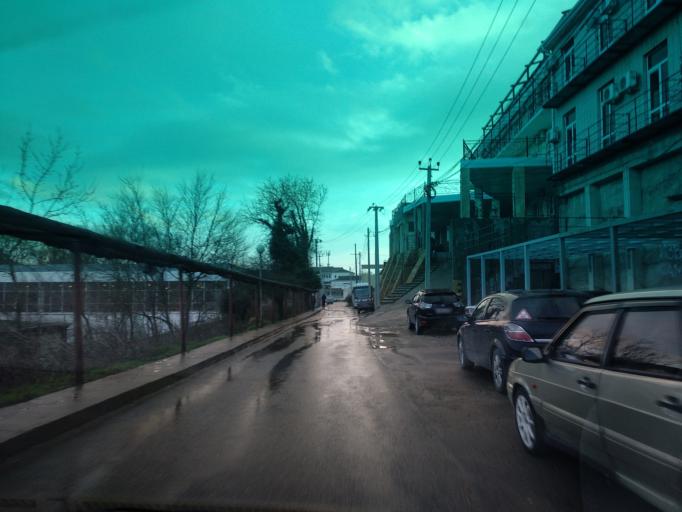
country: RU
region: Krasnodarskiy
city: Novomikhaylovskiy
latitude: 44.2458
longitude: 38.8350
